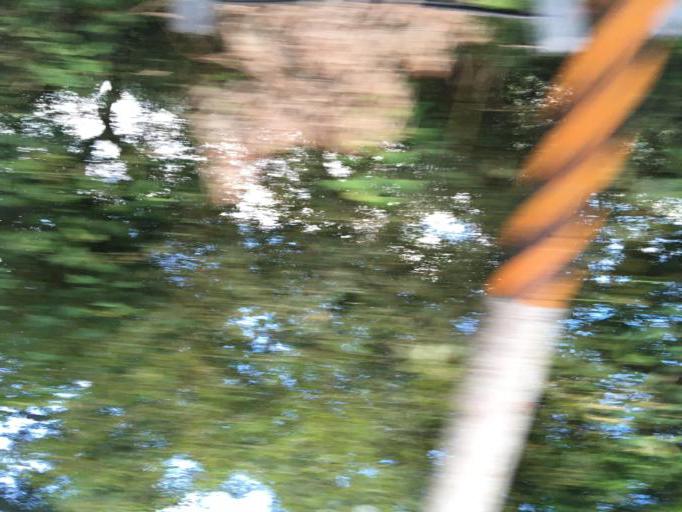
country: TW
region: Taipei
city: Taipei
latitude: 24.9485
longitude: 121.5592
